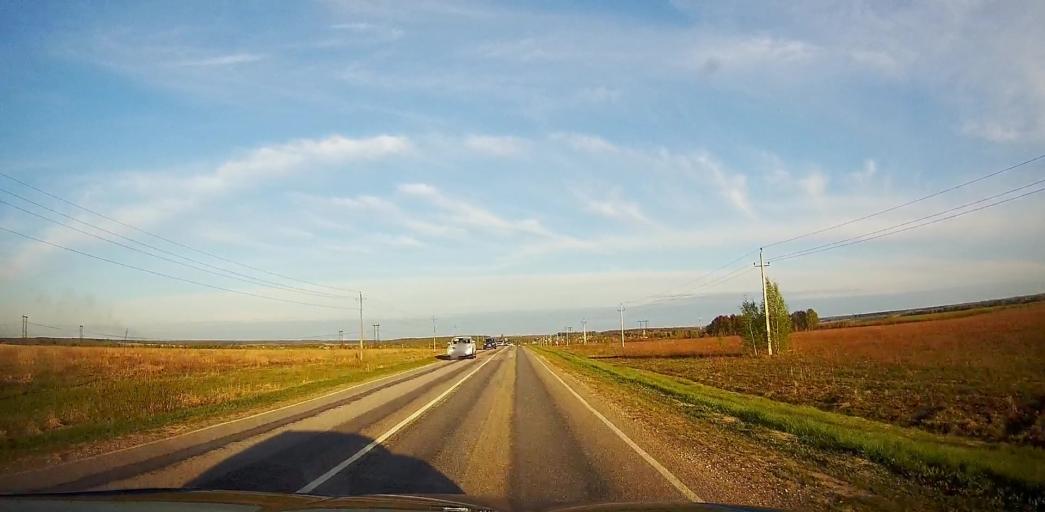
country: RU
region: Moskovskaya
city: Meshcherino
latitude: 55.2670
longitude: 38.2501
